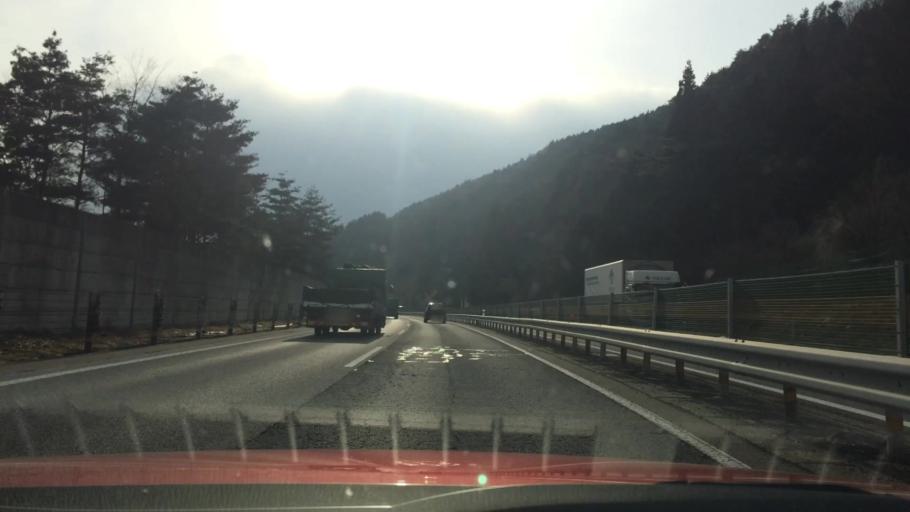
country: JP
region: Nagano
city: Ina
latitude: 35.7700
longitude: 137.9230
